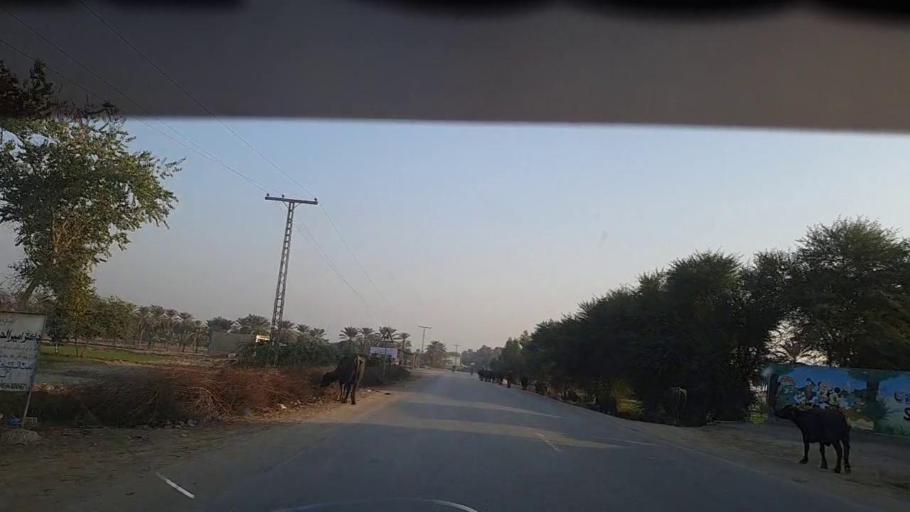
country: PK
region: Sindh
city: Ranipur
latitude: 27.2635
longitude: 68.5238
